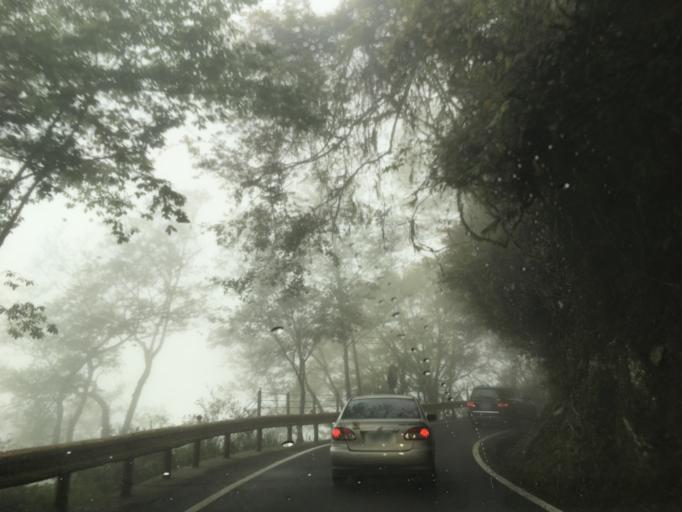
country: TW
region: Taiwan
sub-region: Hualien
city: Hualian
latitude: 24.1863
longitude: 121.4153
